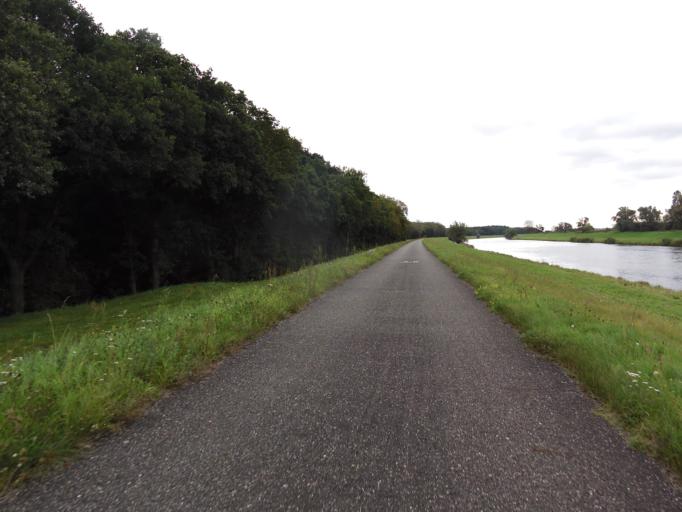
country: DE
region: Brandenburg
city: Bad Wilsnack
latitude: 52.8910
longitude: 11.9514
